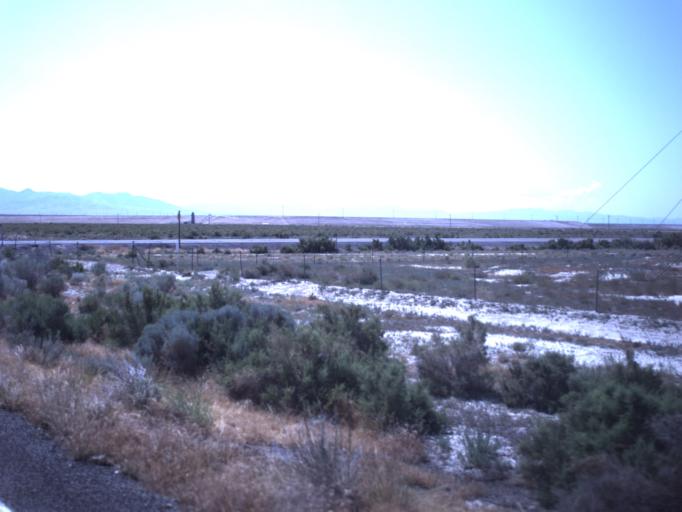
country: US
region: Utah
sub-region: Millard County
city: Delta
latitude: 39.4954
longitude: -112.5792
